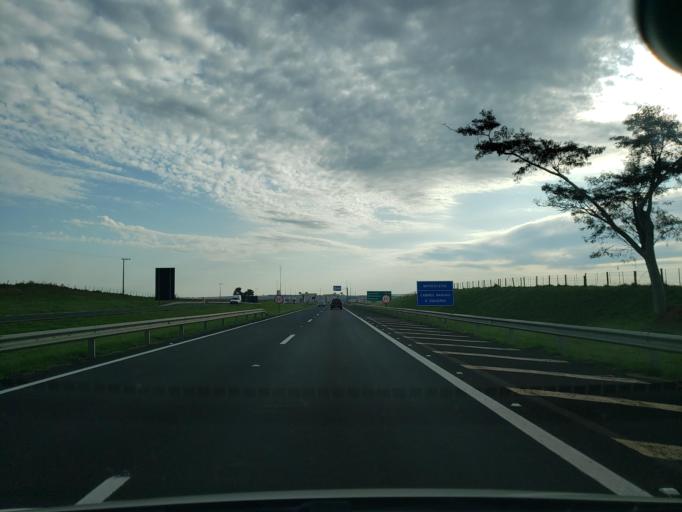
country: BR
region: Sao Paulo
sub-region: Guararapes
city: Guararapes
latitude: -21.2107
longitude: -50.7278
